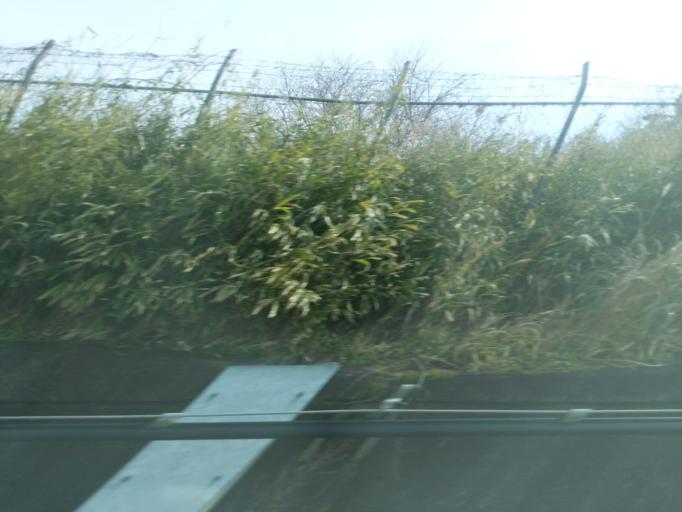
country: JP
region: Miyagi
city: Furukawa
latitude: 38.6661
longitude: 141.0249
